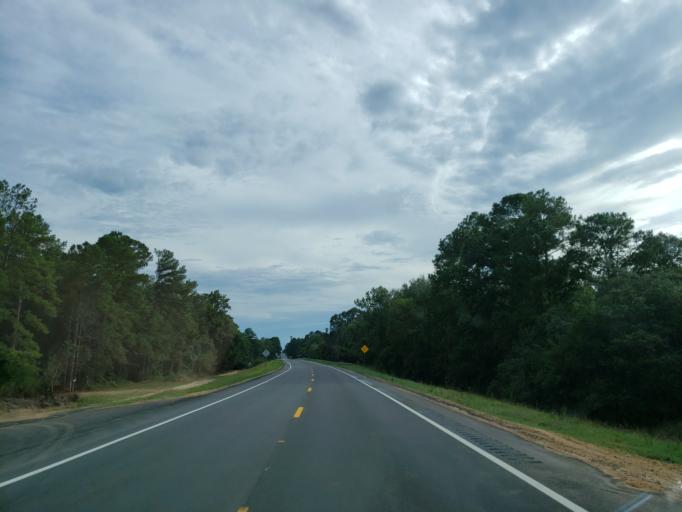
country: US
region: Georgia
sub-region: Berrien County
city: Enigma
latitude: 31.5350
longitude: -83.3965
